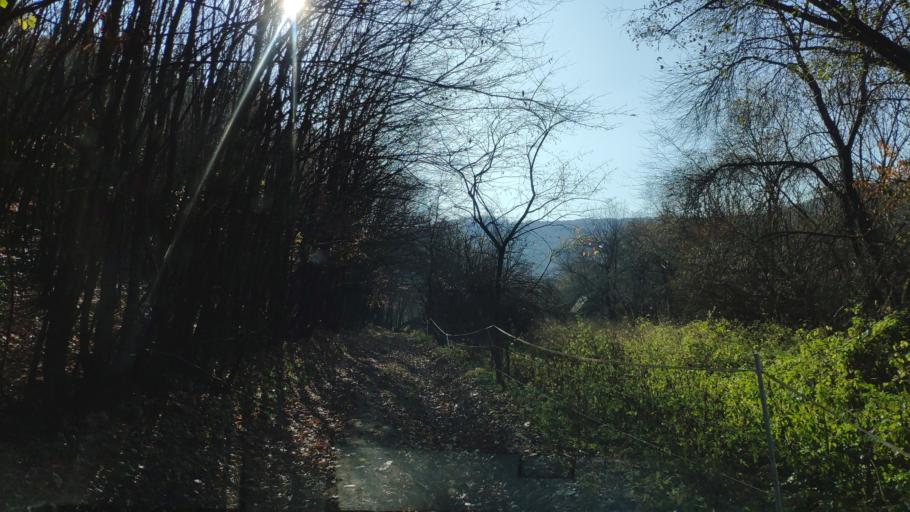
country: SK
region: Presovsky
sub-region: Okres Presov
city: Presov
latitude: 48.9004
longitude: 21.2057
